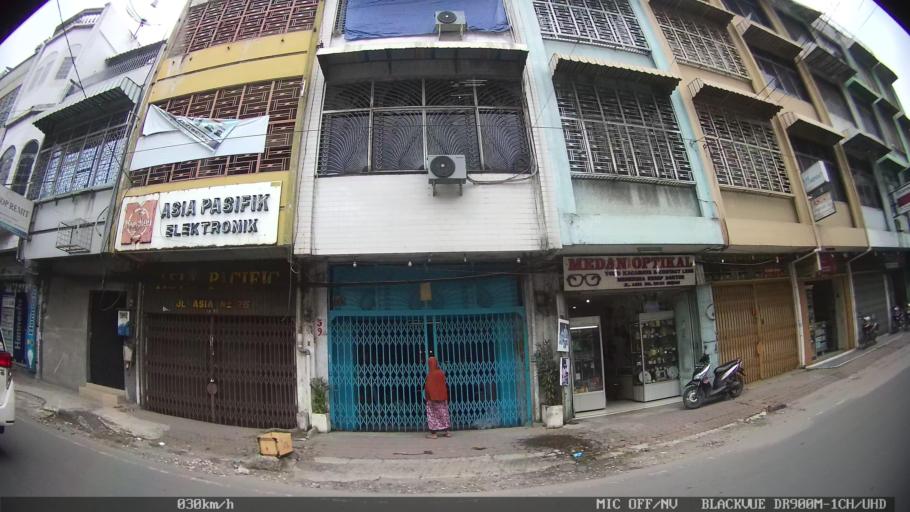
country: ID
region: North Sumatra
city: Medan
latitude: 3.5838
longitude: 98.6895
